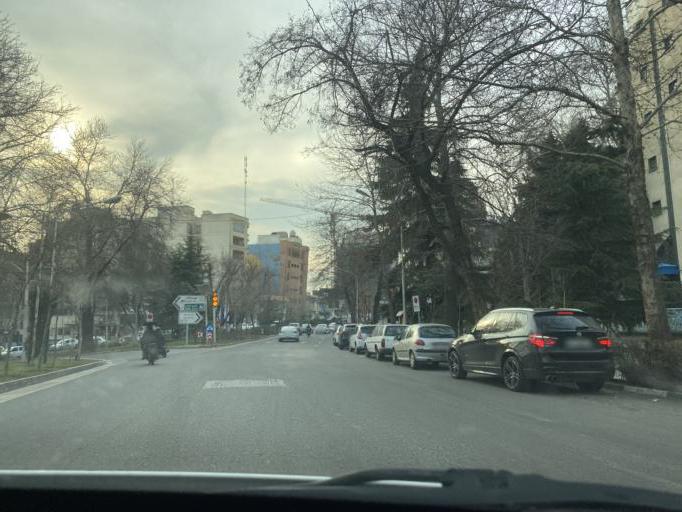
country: IR
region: Tehran
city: Tajrish
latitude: 35.8112
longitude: 51.4701
